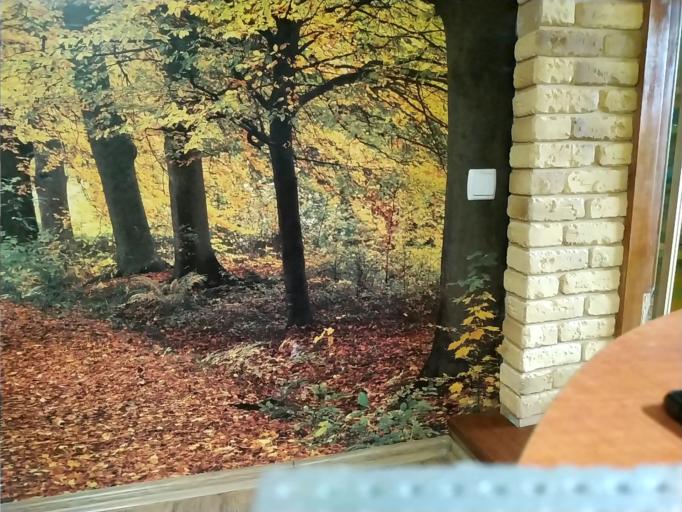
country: RU
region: Vladimir
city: Bavleny
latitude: 56.3666
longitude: 39.5504
